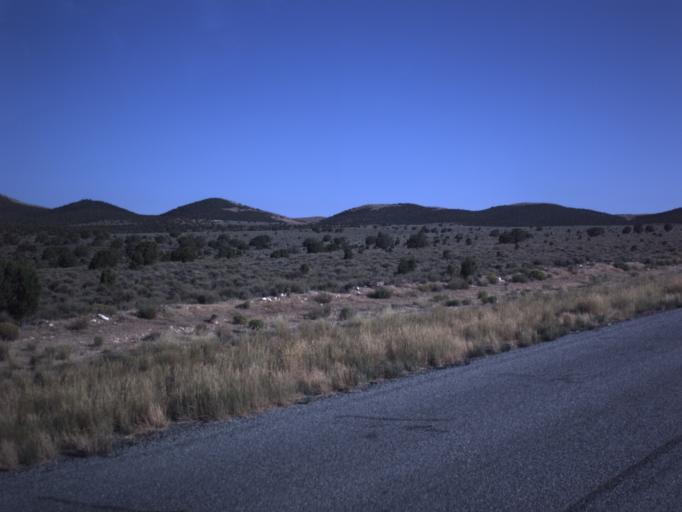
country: US
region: Utah
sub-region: Iron County
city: Parowan
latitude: 38.0222
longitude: -112.9981
